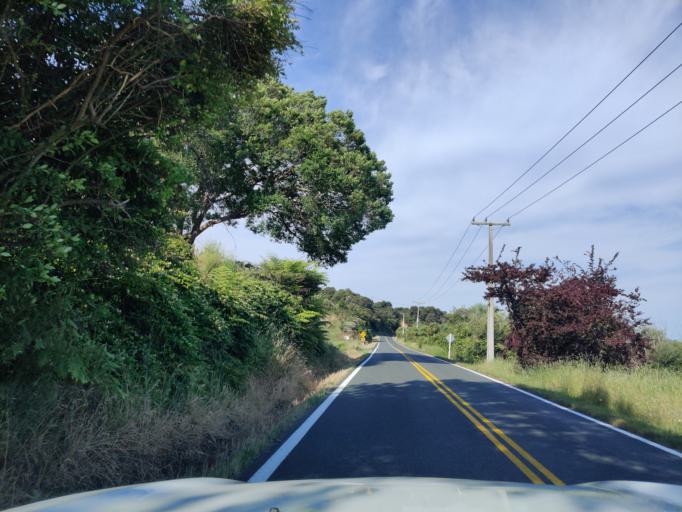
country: NZ
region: Waikato
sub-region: Waikato District
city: Ngaruawahia
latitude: -37.6332
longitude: 175.1544
